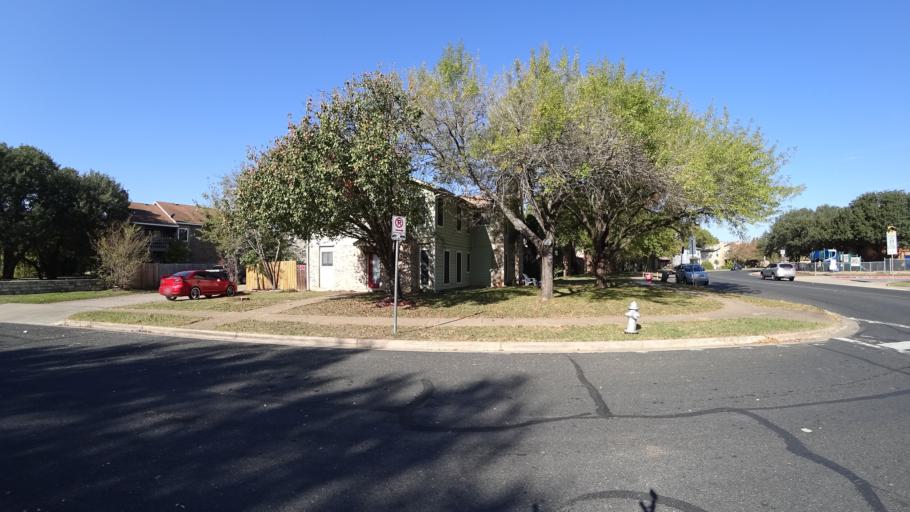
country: US
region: Texas
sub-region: Travis County
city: Barton Creek
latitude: 30.2310
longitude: -97.8458
